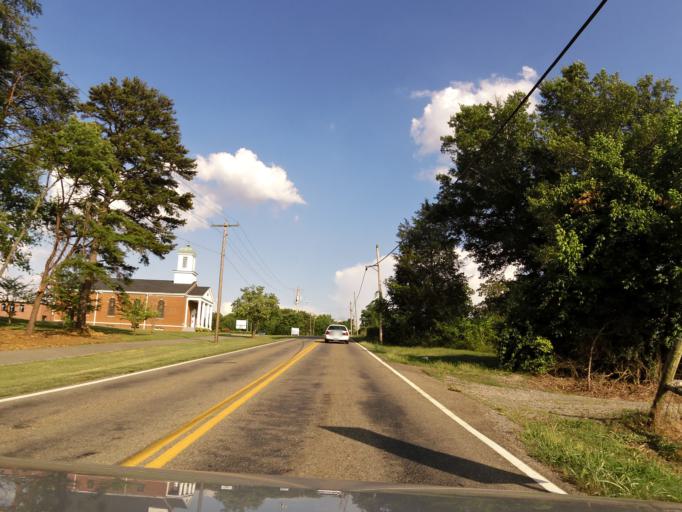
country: US
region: Tennessee
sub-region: Blount County
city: Alcoa
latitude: 35.7885
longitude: -83.9727
